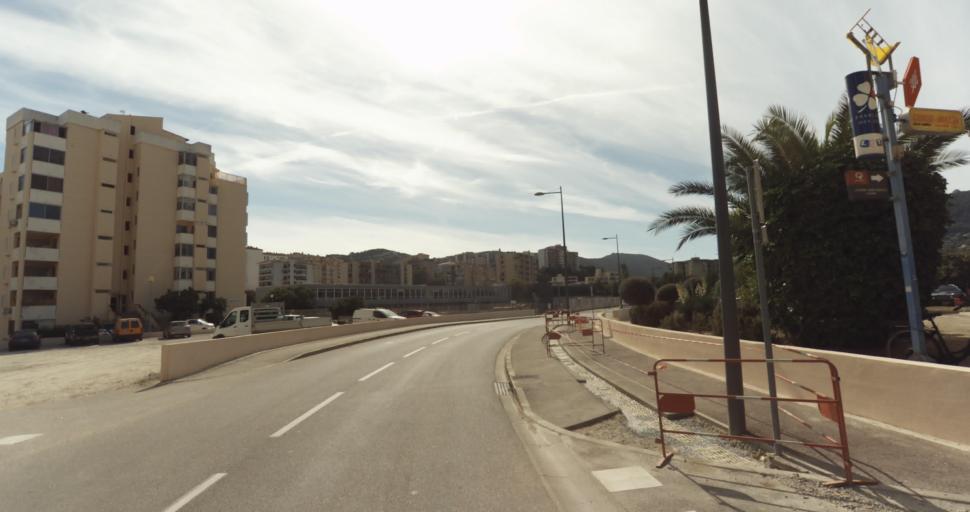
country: FR
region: Corsica
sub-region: Departement de la Corse-du-Sud
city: Ajaccio
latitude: 41.9365
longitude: 8.7397
